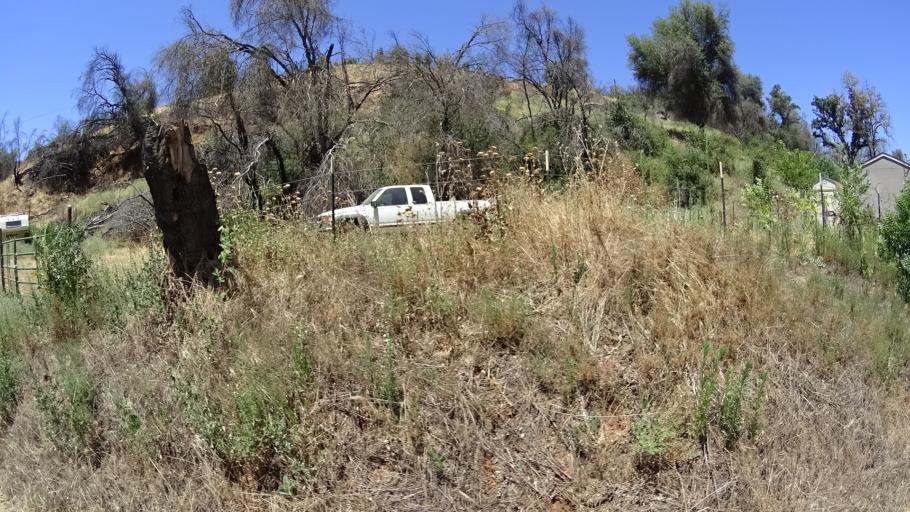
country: US
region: California
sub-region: Calaveras County
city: San Andreas
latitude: 38.2830
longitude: -120.6688
